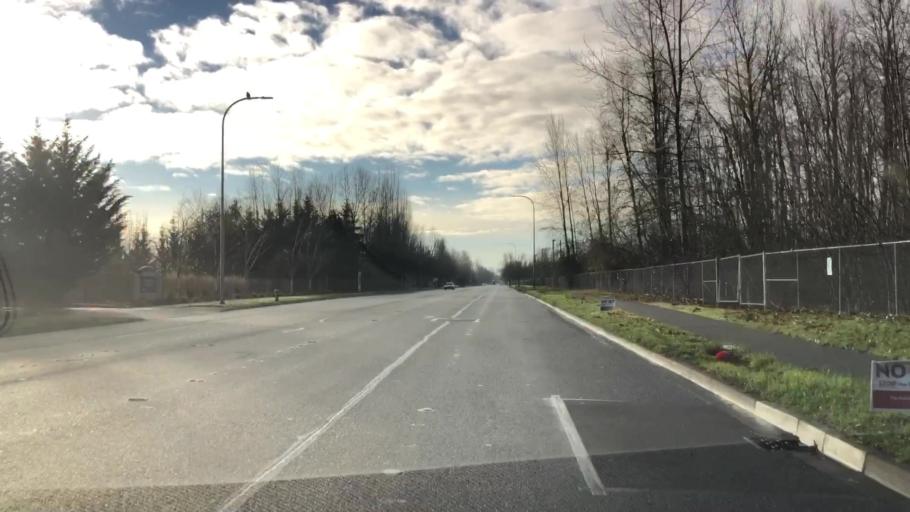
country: US
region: Washington
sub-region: King County
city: Renton
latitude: 47.4520
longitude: -122.2328
